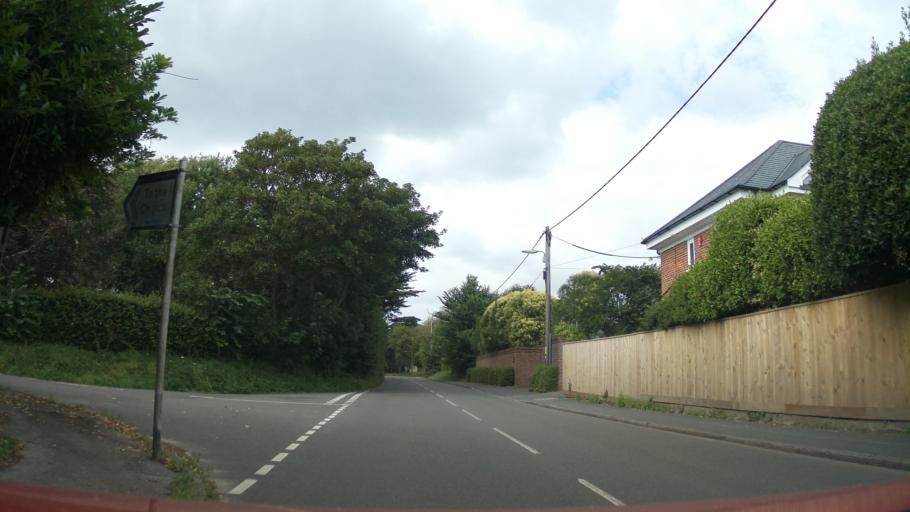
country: GB
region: England
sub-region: Hampshire
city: Milford on Sea
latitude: 50.7280
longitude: -1.5878
